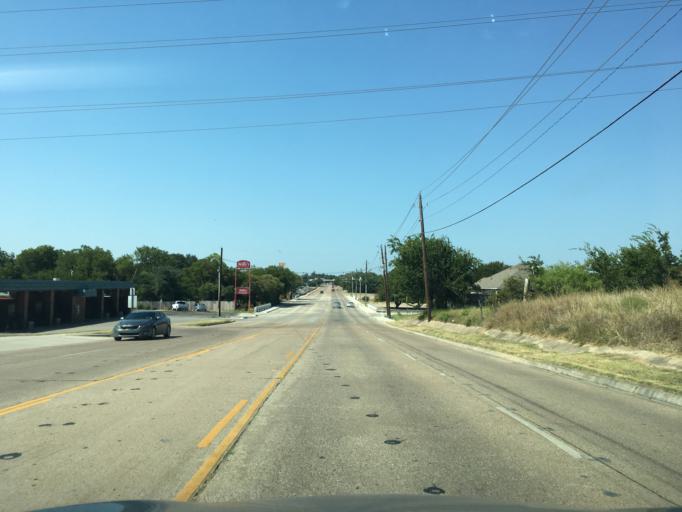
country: US
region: Texas
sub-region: Tarrant County
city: Forest Hill
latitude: 32.6532
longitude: -97.2699
